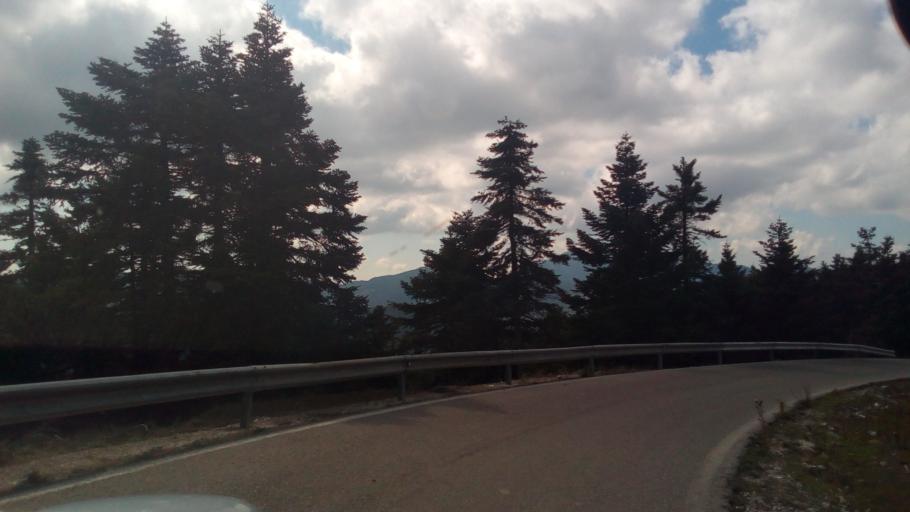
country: GR
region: West Greece
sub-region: Nomos Aitolias kai Akarnanias
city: Nafpaktos
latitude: 38.6387
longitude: 21.9387
